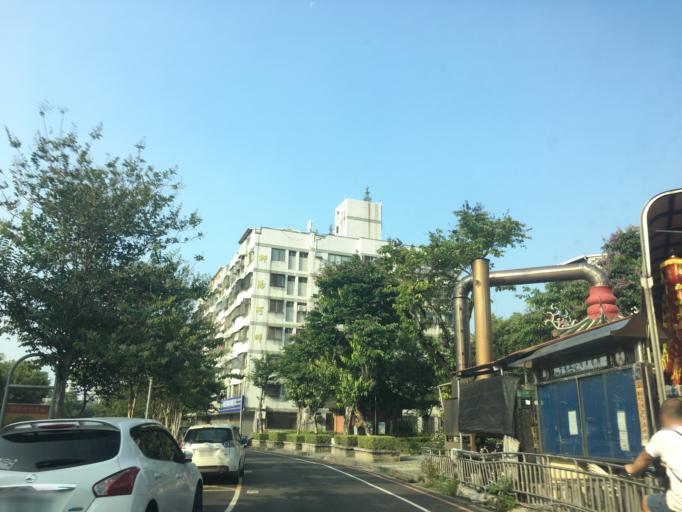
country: TW
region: Taiwan
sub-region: Taichung City
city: Taichung
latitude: 24.1691
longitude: 120.6894
